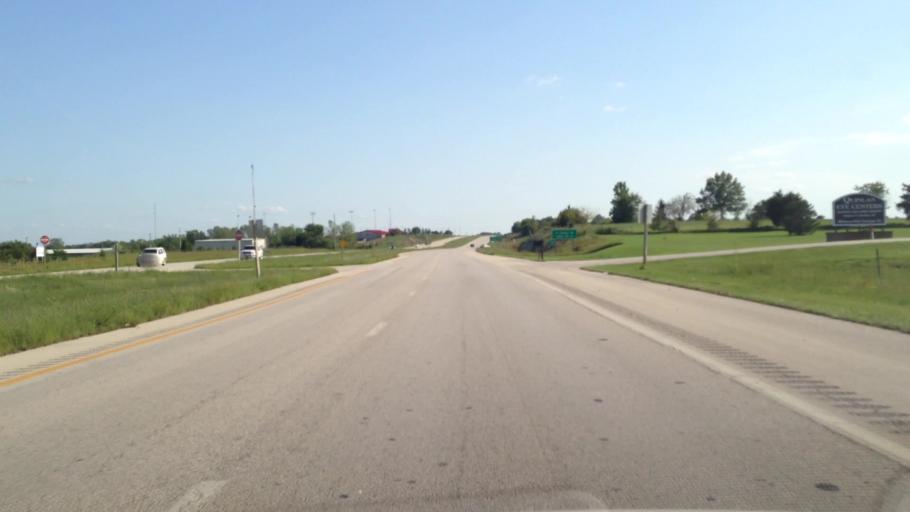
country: US
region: Kansas
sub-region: Bourbon County
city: Fort Scott
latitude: 37.7939
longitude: -94.7050
